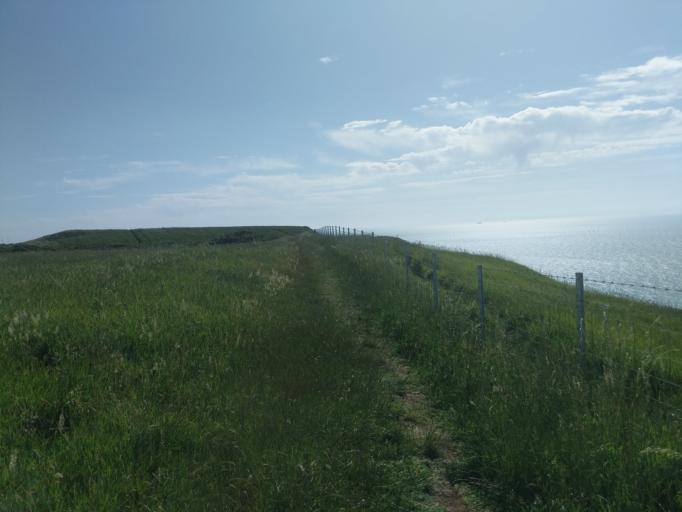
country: GB
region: England
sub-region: Kent
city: Dover
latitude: 51.1024
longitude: 1.2493
